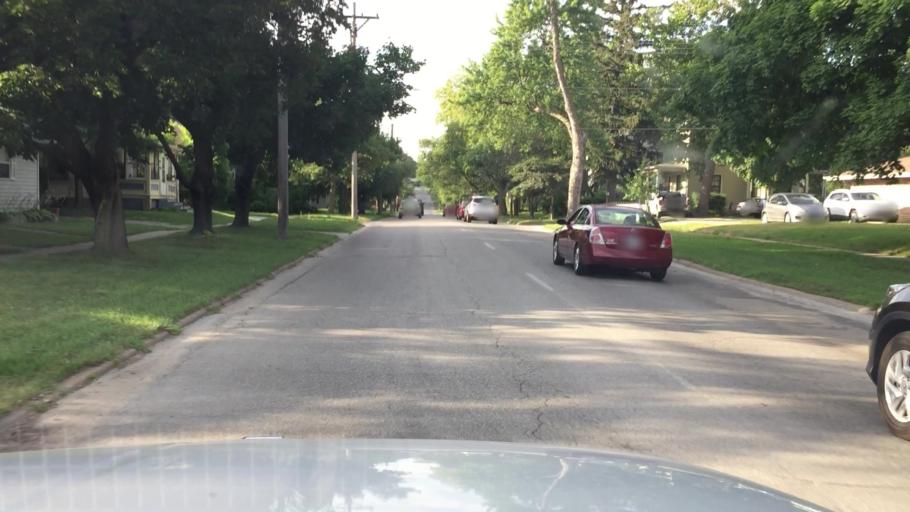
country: US
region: Iowa
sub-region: Johnson County
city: Iowa City
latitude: 41.6637
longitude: -91.5229
